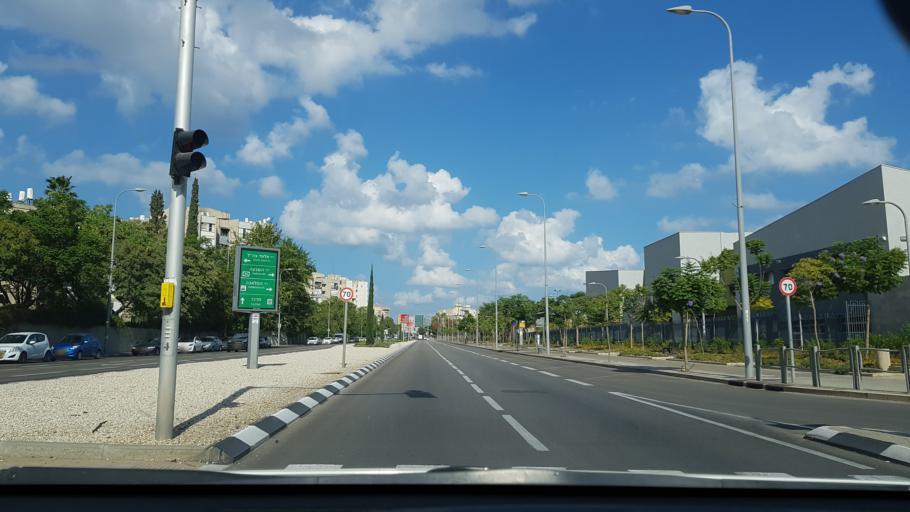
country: IL
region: Tel Aviv
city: Holon
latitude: 32.0074
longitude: 34.7978
